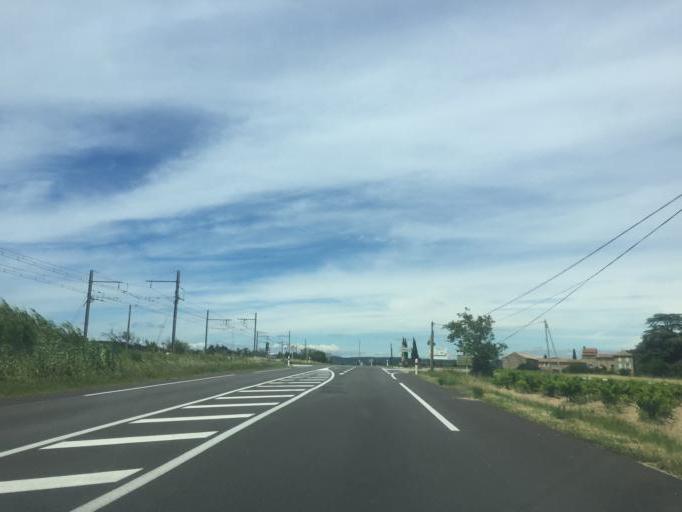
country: FR
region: Languedoc-Roussillon
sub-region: Departement du Gard
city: Orsan
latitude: 44.1433
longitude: 4.6614
